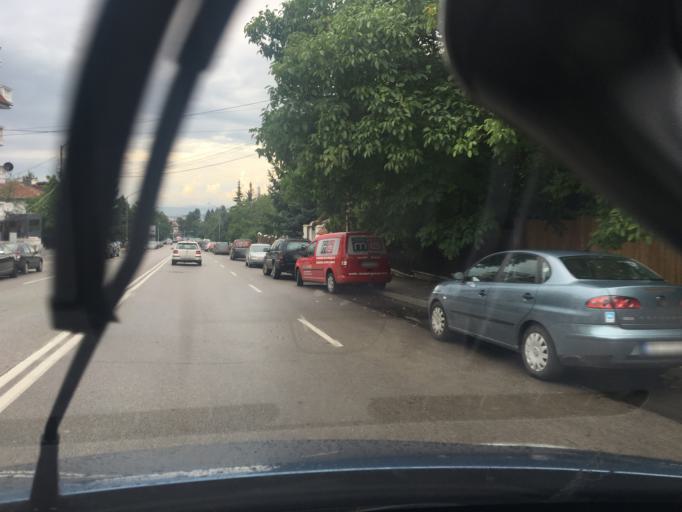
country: BG
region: Sofia-Capital
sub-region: Stolichna Obshtina
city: Sofia
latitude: 42.6560
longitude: 23.2654
